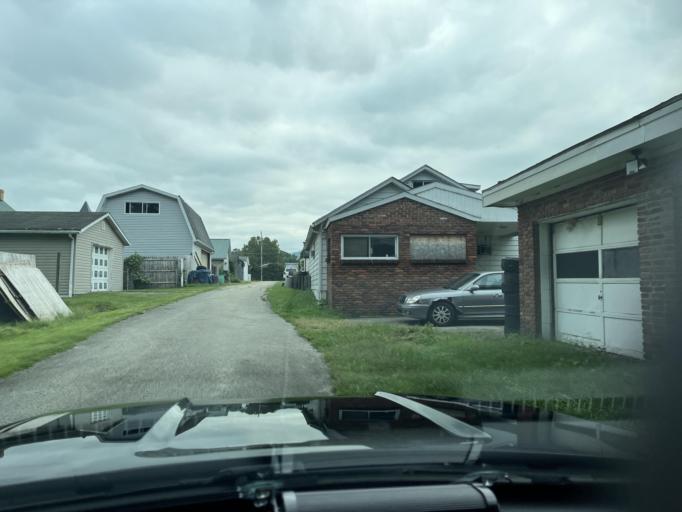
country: US
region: Pennsylvania
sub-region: Fayette County
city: Hopwood
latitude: 39.8741
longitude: -79.7020
